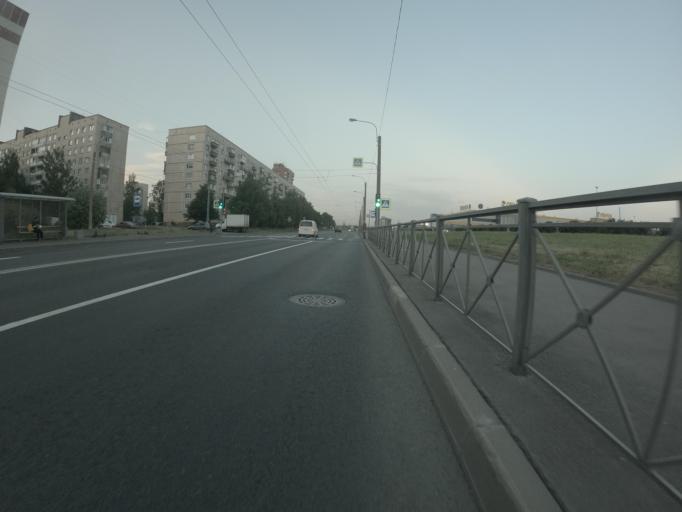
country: RU
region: St.-Petersburg
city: Krasnogvargeisky
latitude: 59.9356
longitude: 30.4949
